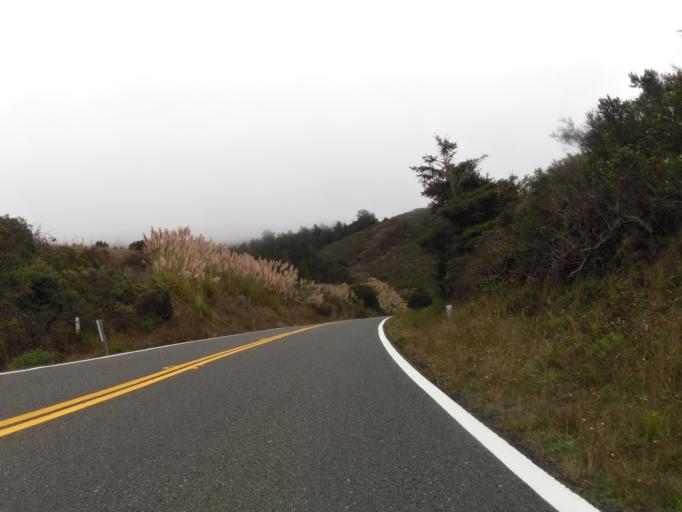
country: US
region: California
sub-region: Sonoma County
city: Monte Rio
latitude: 38.4588
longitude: -123.1377
